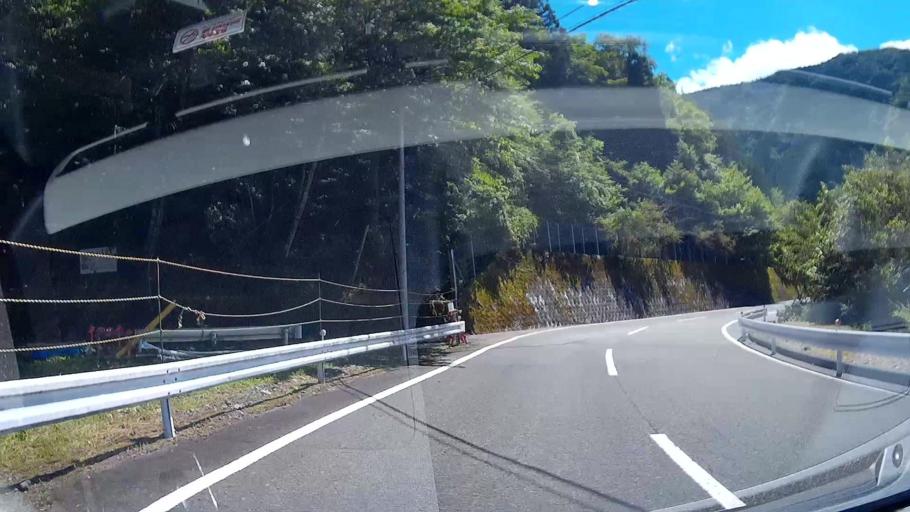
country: JP
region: Shizuoka
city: Shizuoka-shi
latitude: 35.1928
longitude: 138.2427
